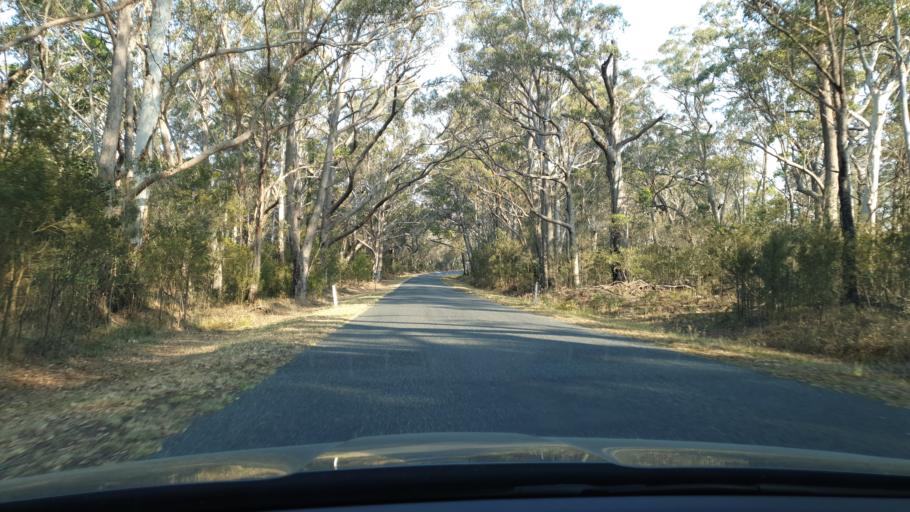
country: AU
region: New South Wales
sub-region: Tenterfield Municipality
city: Carrolls Creek
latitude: -28.6992
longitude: 152.0958
